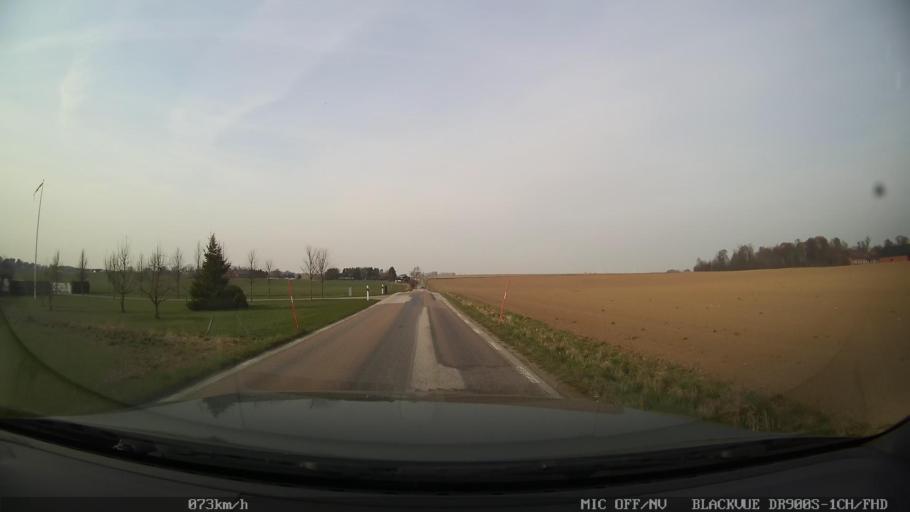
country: SE
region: Skane
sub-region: Ystads Kommun
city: Ystad
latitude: 55.4509
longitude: 13.8312
